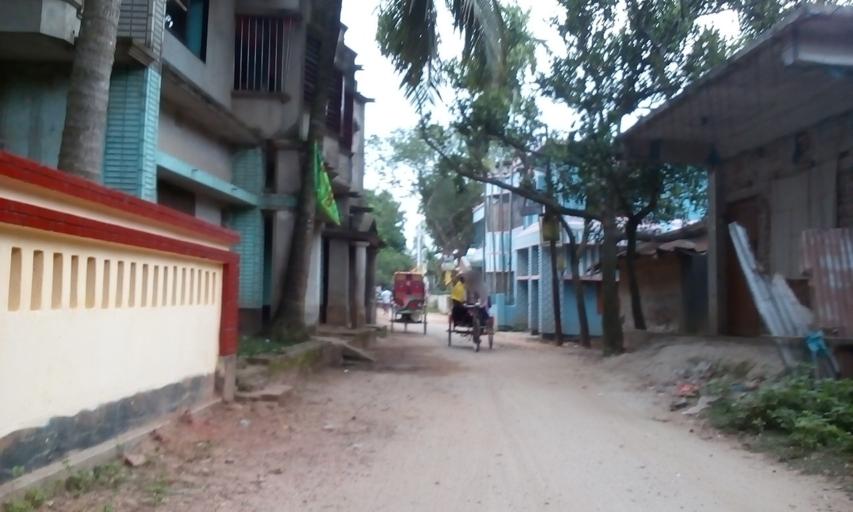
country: IN
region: West Bengal
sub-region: Dakshin Dinajpur
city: Balurghat
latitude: 25.3844
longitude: 88.9934
